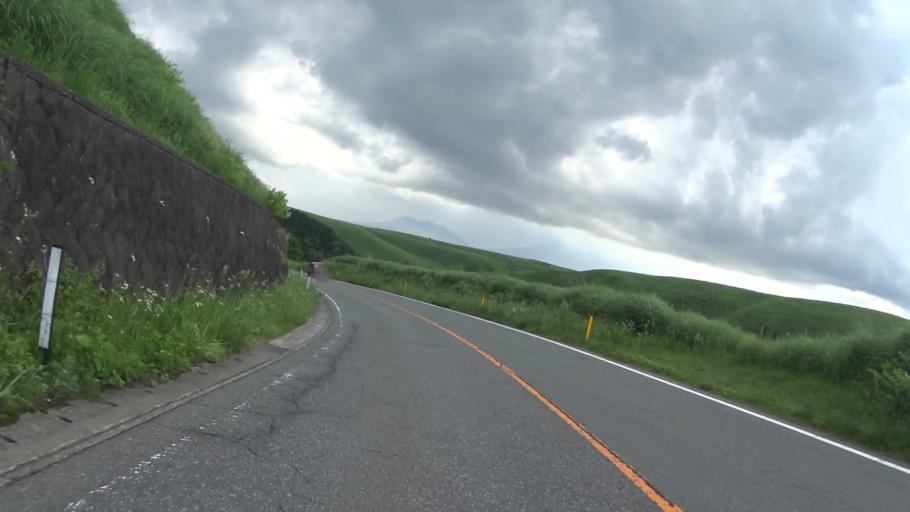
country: JP
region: Kumamoto
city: Aso
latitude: 33.0159
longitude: 131.1533
